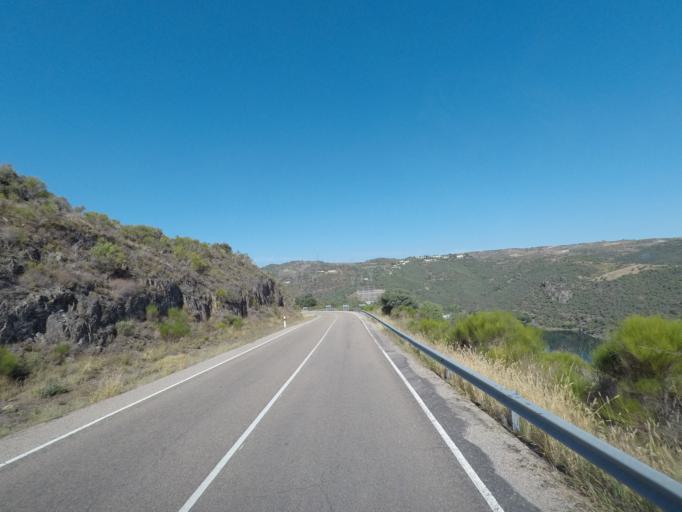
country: ES
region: Castille and Leon
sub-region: Provincia de Salamanca
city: Villarino de los Aires
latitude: 41.2966
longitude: -6.4643
